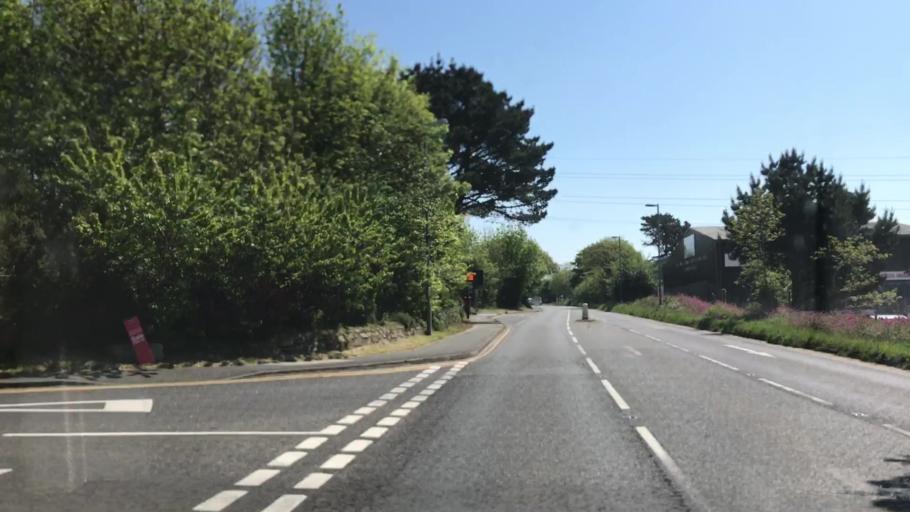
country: GB
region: England
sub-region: Cornwall
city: Chacewater
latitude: 50.2640
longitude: -5.1244
